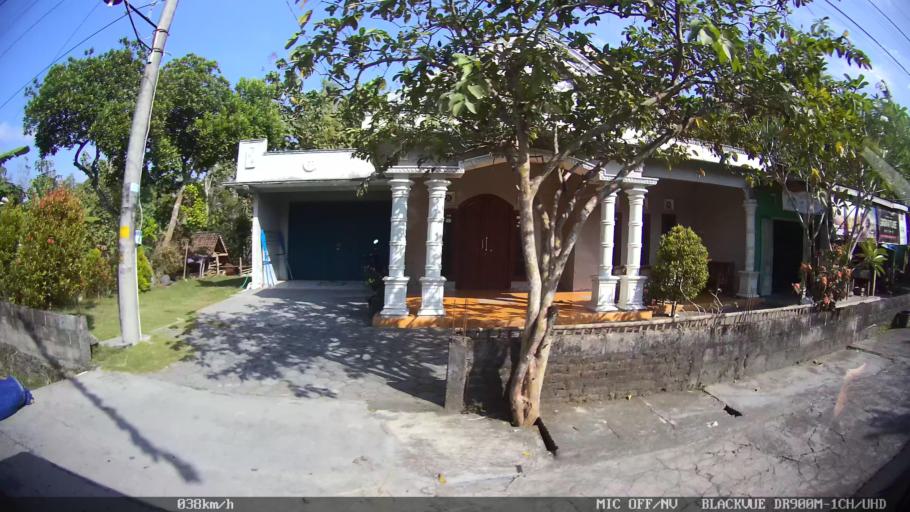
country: ID
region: Daerah Istimewa Yogyakarta
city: Kasihan
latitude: -7.8190
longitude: 110.2938
